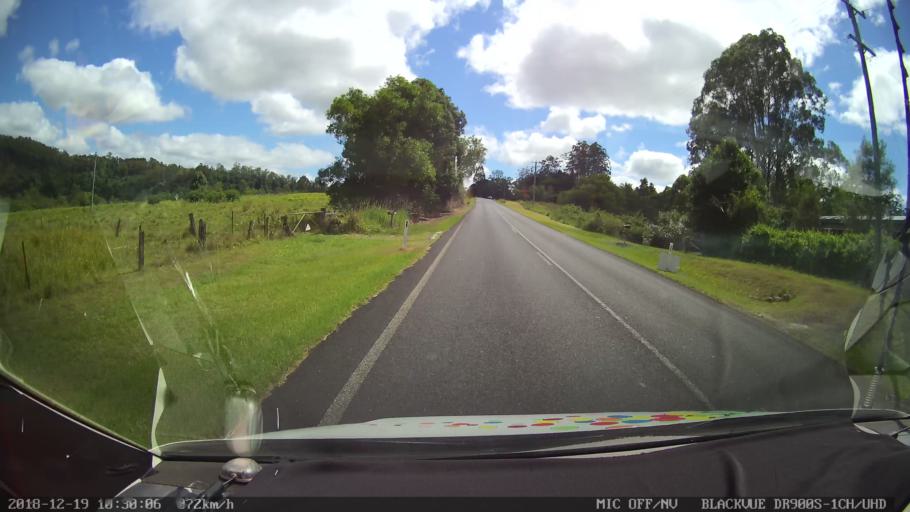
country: AU
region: New South Wales
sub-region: Lismore Municipality
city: Larnook
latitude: -28.5909
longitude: 153.1043
